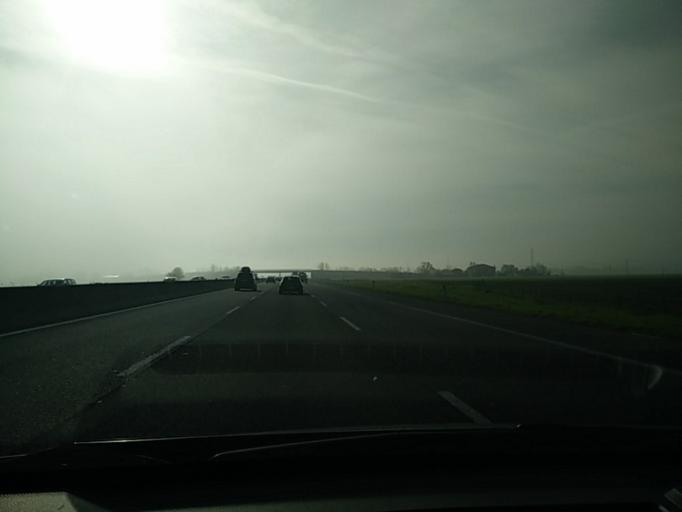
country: IT
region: Emilia-Romagna
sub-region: Provincia di Bologna
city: Osteria Grande
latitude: 44.4517
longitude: 11.5391
